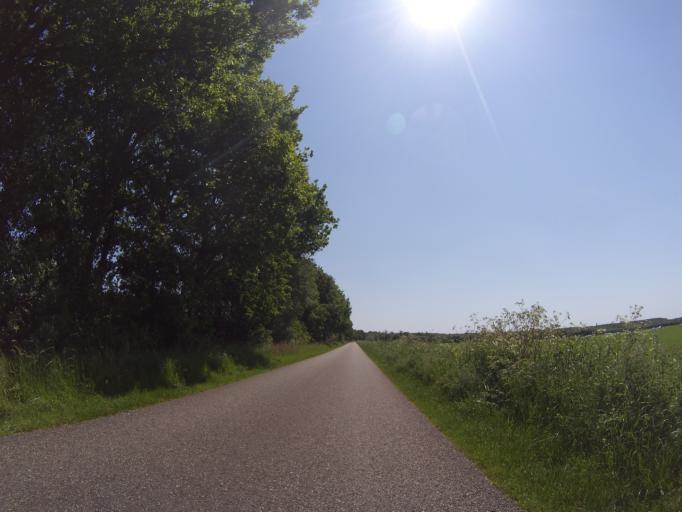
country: NL
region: Drenthe
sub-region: Gemeente Emmen
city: Schoonebeek
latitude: 52.7038
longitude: 6.8309
